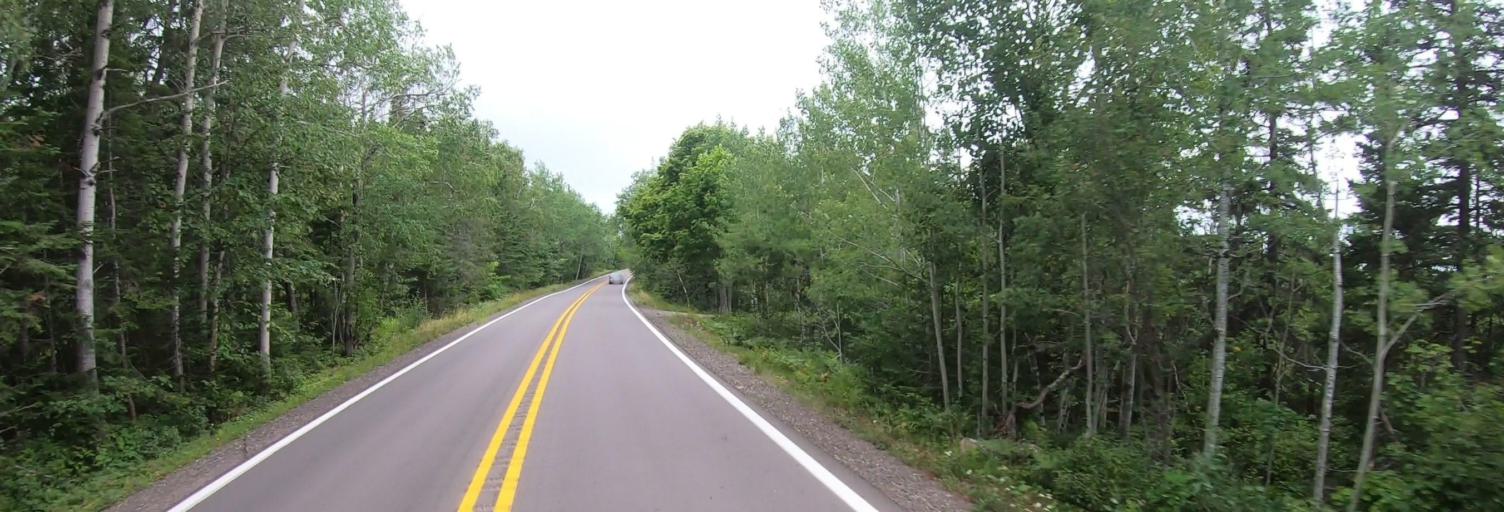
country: US
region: Michigan
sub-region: Keweenaw County
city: Eagle River
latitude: 47.4770
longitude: -88.0000
